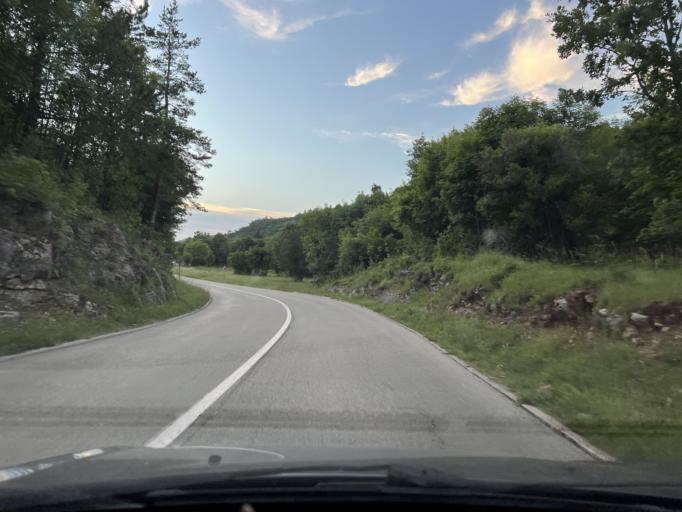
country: HR
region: Primorsko-Goranska
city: Klana
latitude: 45.4637
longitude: 14.3076
